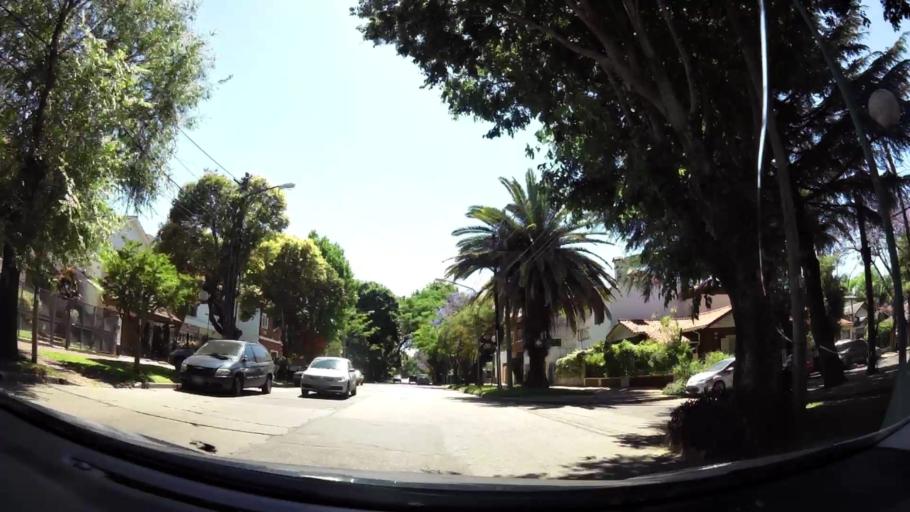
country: AR
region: Buenos Aires
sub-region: Partido de Vicente Lopez
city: Olivos
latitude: -34.4971
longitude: -58.4961
